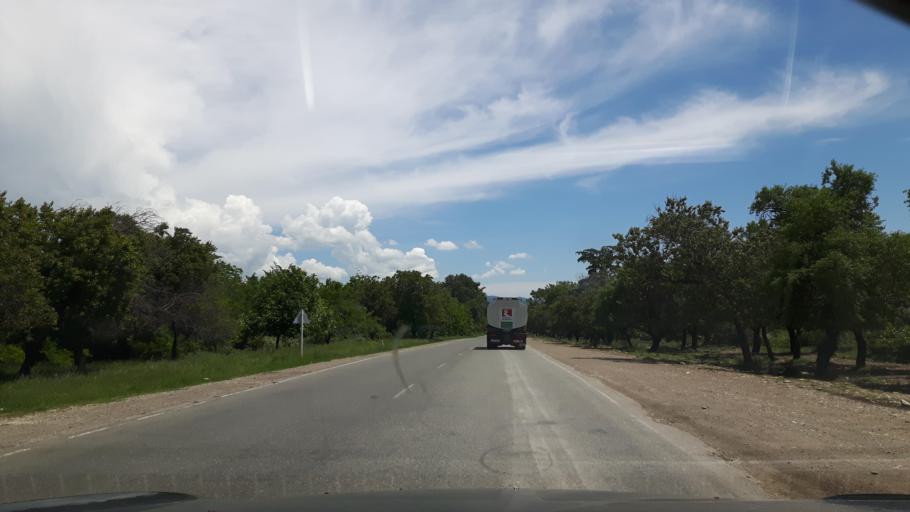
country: GE
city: Didi Lilo
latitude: 41.7094
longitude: 45.1438
